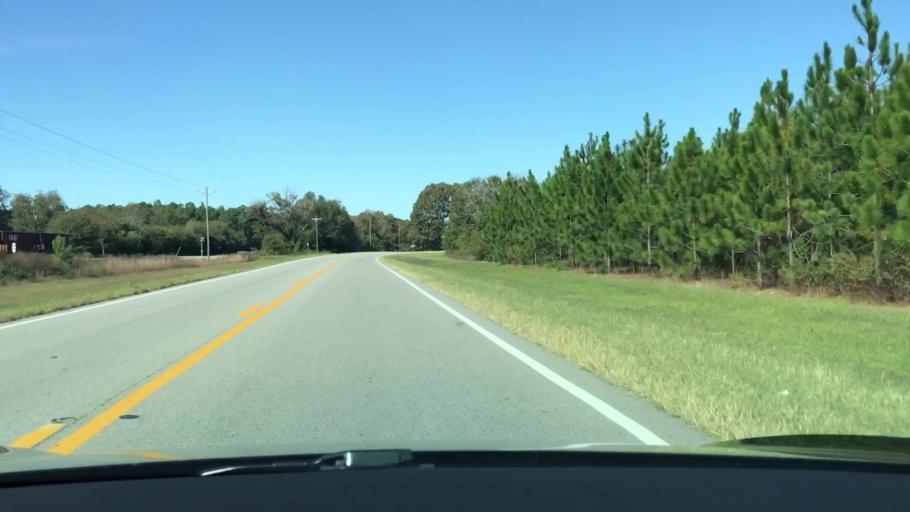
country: US
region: Georgia
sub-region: Glascock County
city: Gibson
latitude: 33.3072
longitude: -82.5305
